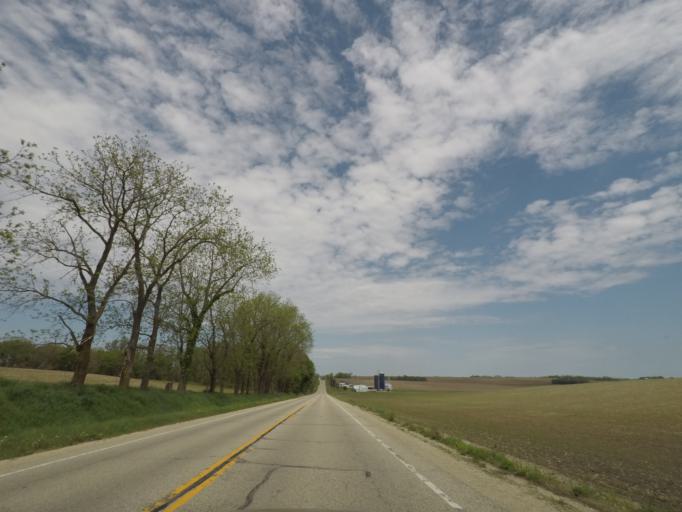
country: US
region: Wisconsin
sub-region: Rock County
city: Orfordville
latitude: 42.6771
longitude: -89.2880
